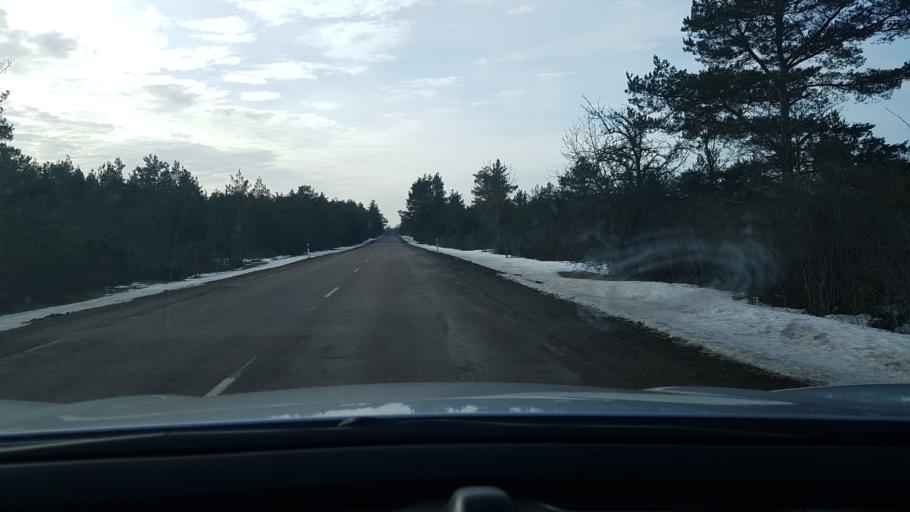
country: EE
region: Saare
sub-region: Kuressaare linn
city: Kuressaare
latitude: 58.3248
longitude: 22.5538
